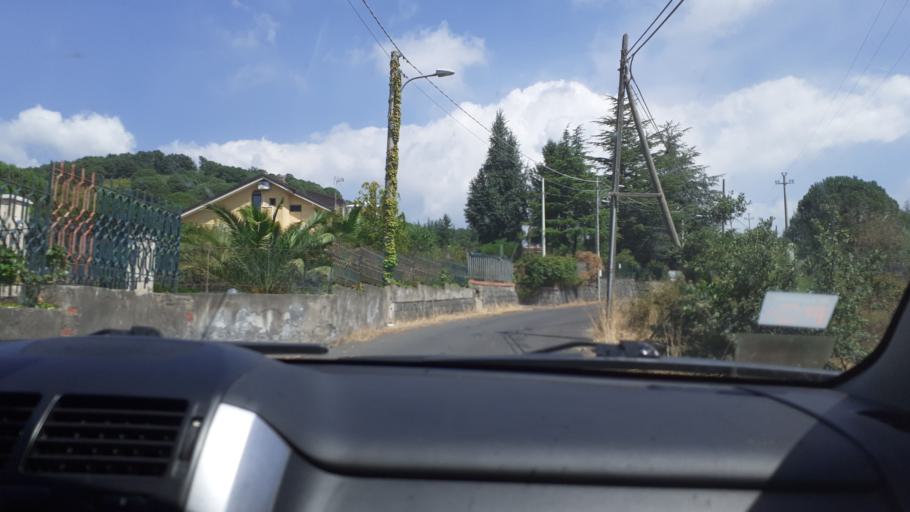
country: IT
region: Sicily
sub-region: Catania
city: Nicolosi
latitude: 37.6313
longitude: 15.0245
